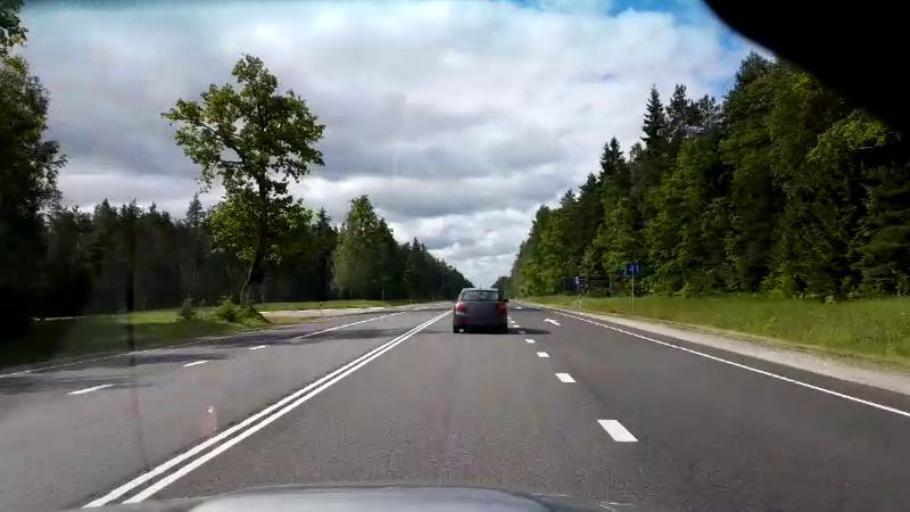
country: EE
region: Raplamaa
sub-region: Maerjamaa vald
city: Marjamaa
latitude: 58.8778
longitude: 24.4468
